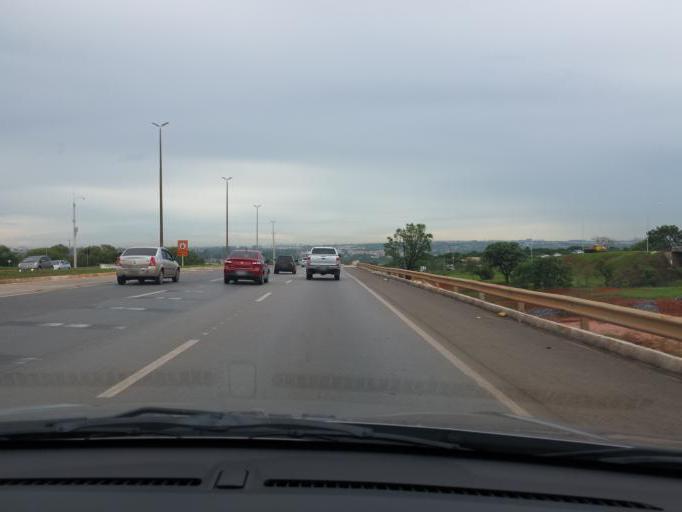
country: BR
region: Federal District
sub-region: Brasilia
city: Brasilia
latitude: -15.8849
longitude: -47.9602
